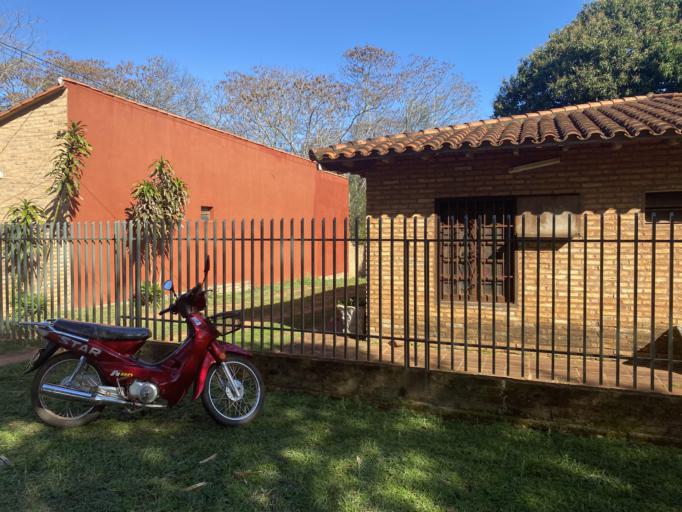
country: PY
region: Misiones
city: San Juan Bautista
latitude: -26.6655
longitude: -57.1373
